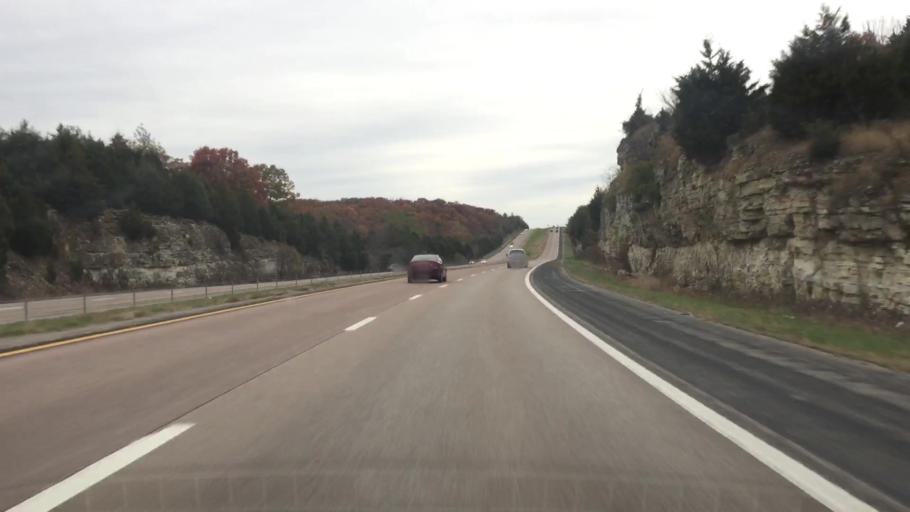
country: US
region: Missouri
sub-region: Boone County
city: Ashland
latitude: 38.6847
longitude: -92.2550
